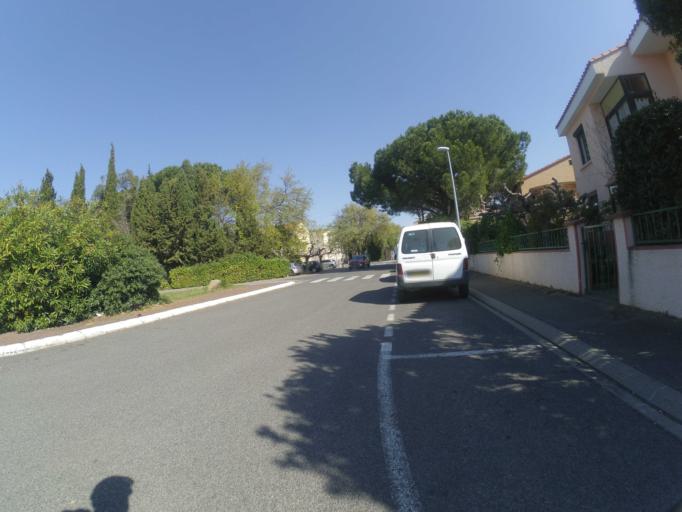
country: FR
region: Languedoc-Roussillon
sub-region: Departement des Pyrenees-Orientales
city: Thuir
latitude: 42.6294
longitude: 2.7588
